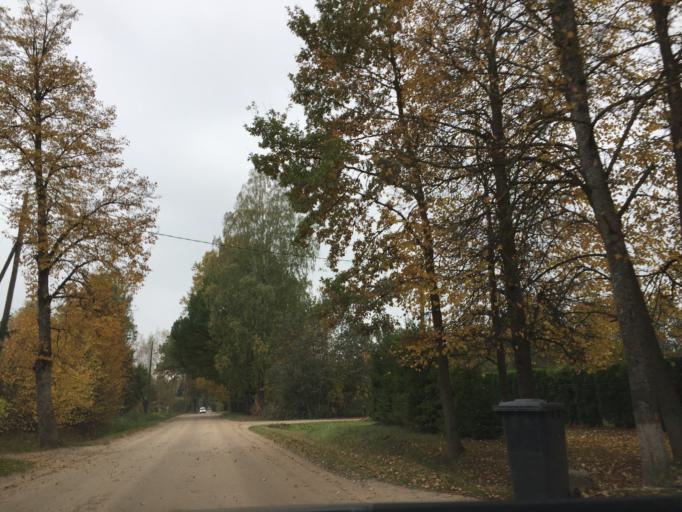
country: LV
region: Jelgava
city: Jelgava
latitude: 56.6850
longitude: 23.7346
